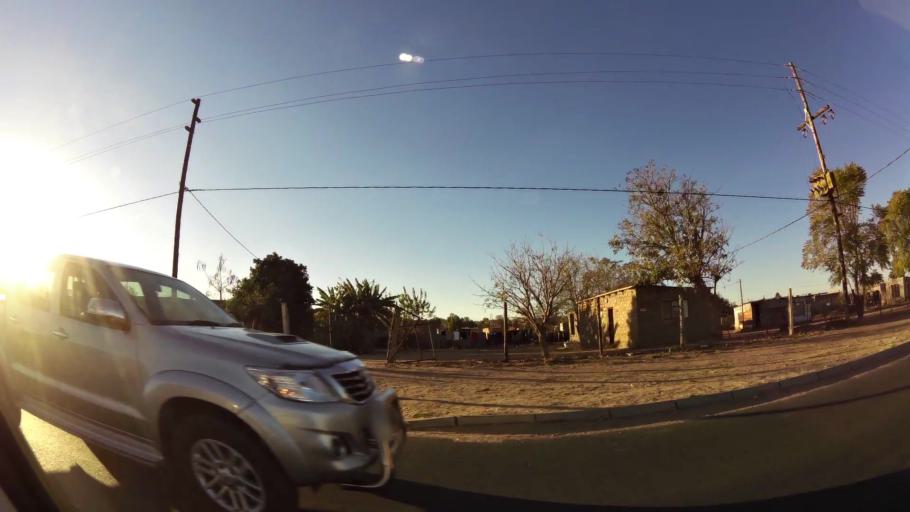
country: ZA
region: Limpopo
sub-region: Capricorn District Municipality
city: Polokwane
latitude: -23.8293
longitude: 29.3771
